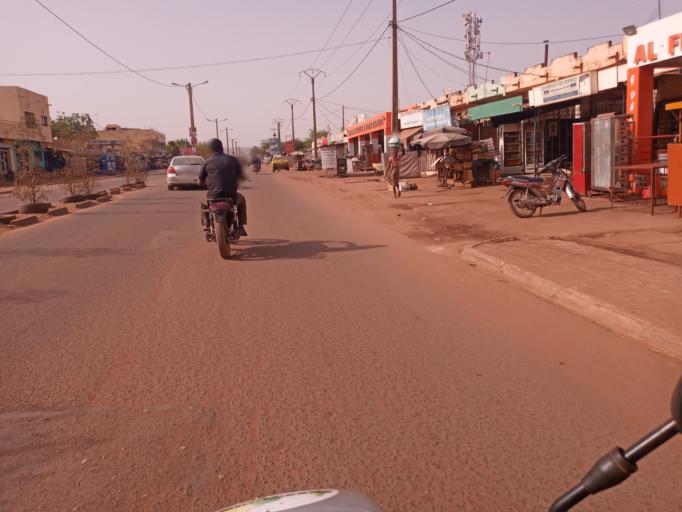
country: ML
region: Bamako
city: Bamako
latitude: 12.6698
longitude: -7.9424
